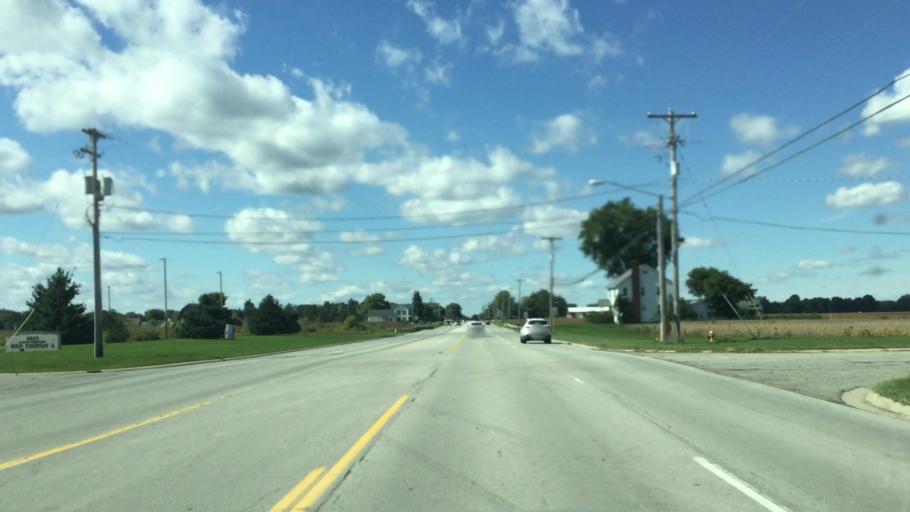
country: US
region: Michigan
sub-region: Genesee County
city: Swartz Creek
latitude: 42.9437
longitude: -83.7512
